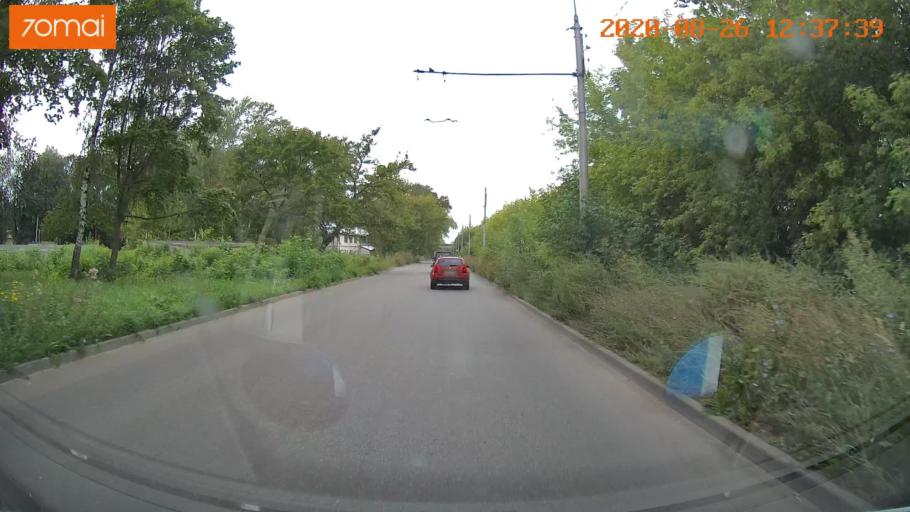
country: RU
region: Rjazan
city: Ryazan'
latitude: 54.6056
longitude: 39.7674
